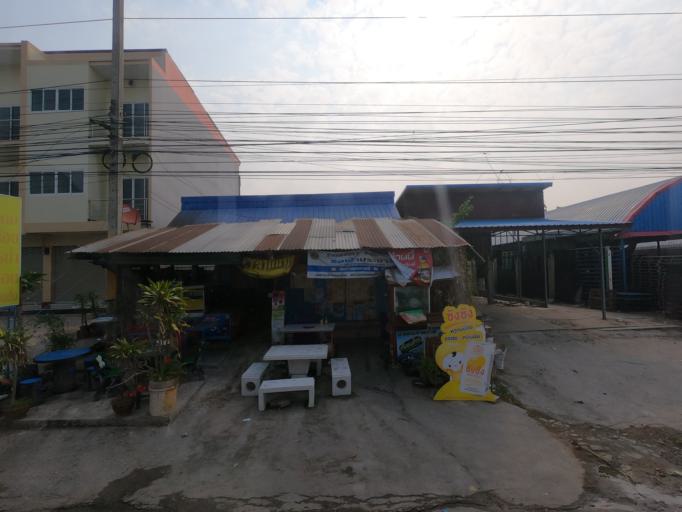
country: TH
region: Khon Kaen
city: Khon Kaen
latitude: 16.3225
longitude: 102.7958
